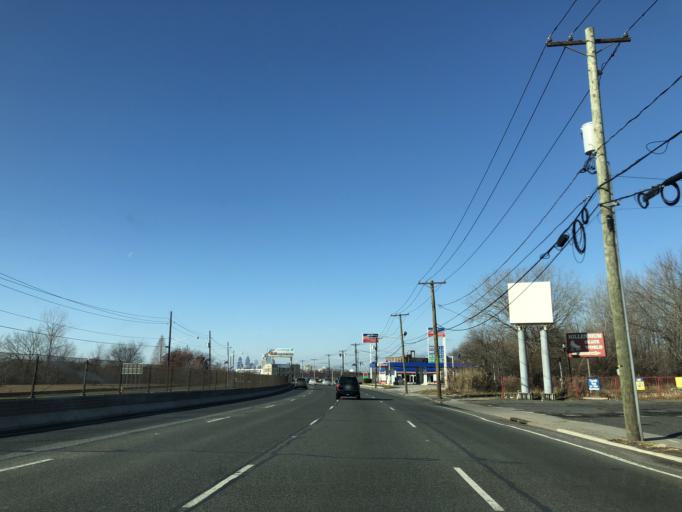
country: US
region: New Jersey
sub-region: Camden County
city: Wood-Lynne
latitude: 39.9399
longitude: -75.0951
